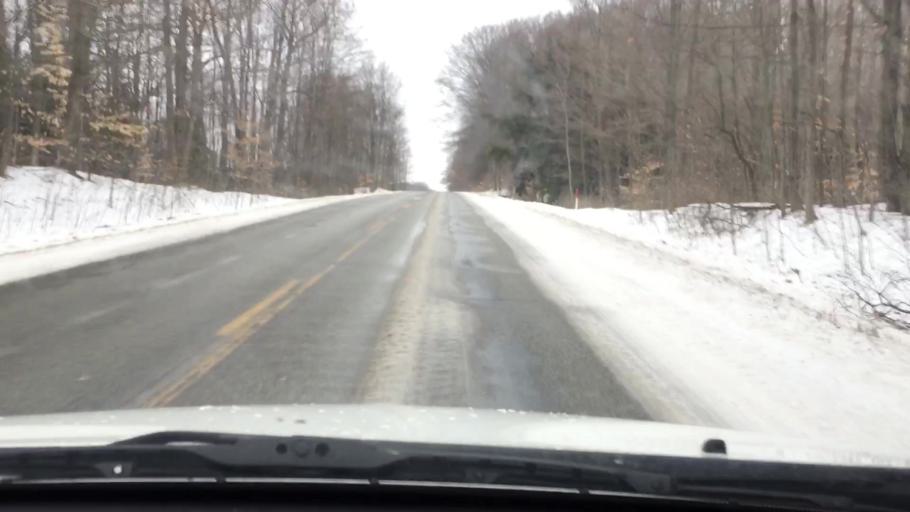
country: US
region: Michigan
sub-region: Wexford County
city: Cadillac
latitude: 44.1839
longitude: -85.4056
